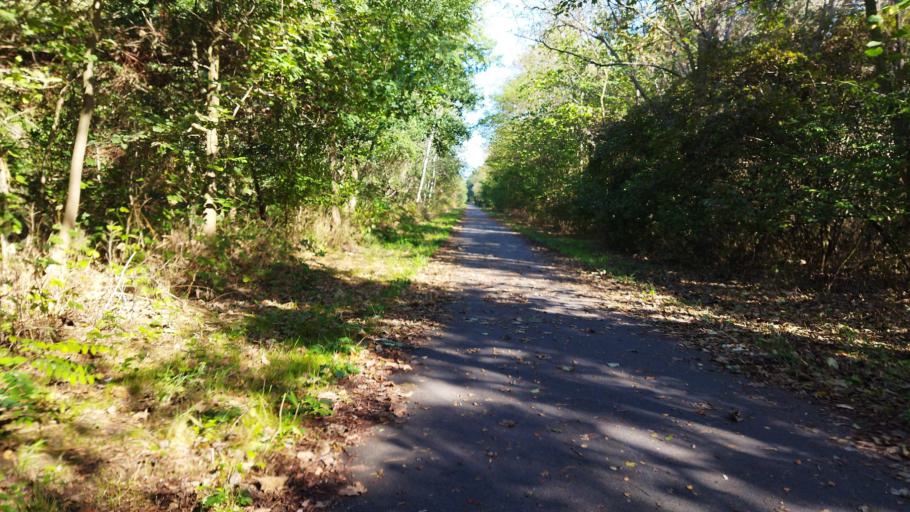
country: DE
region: Lower Saxony
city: Ohne
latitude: 52.2666
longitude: 7.3139
